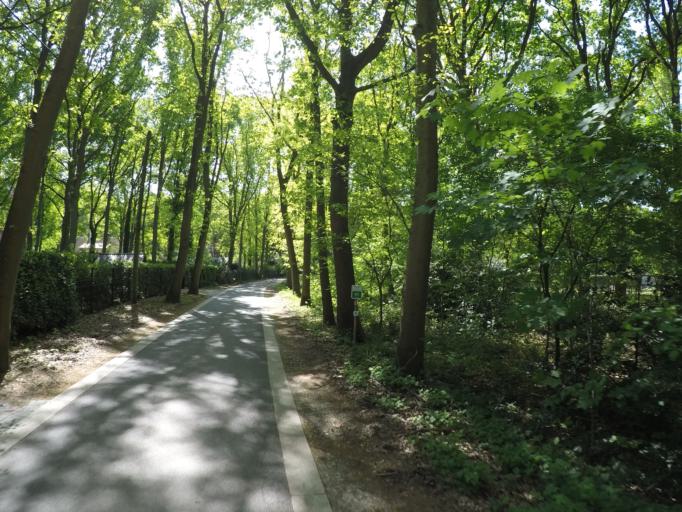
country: BE
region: Flanders
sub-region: Provincie Antwerpen
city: Zoersel
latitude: 51.2585
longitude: 4.7038
